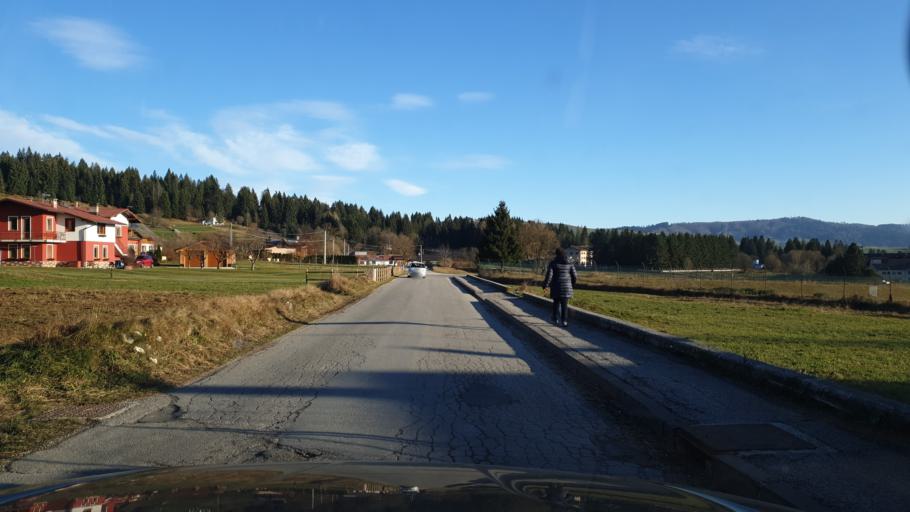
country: IT
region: Veneto
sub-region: Provincia di Vicenza
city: Gallio
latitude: 45.8892
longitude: 11.5215
